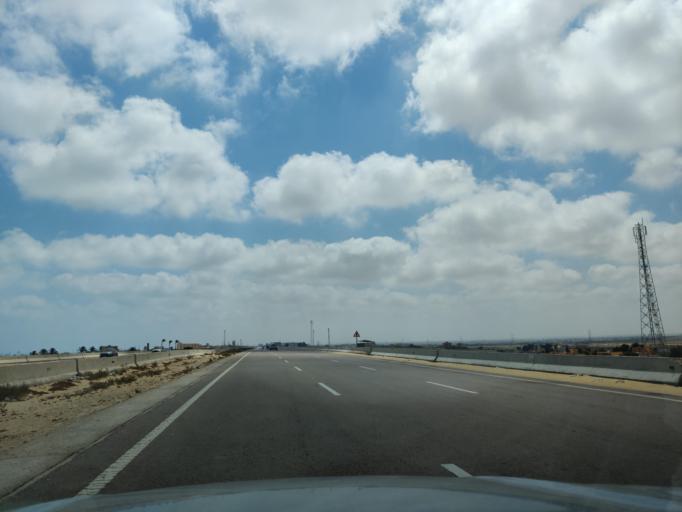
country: EG
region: Muhafazat Matruh
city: Al `Alamayn
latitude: 30.8153
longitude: 29.1332
